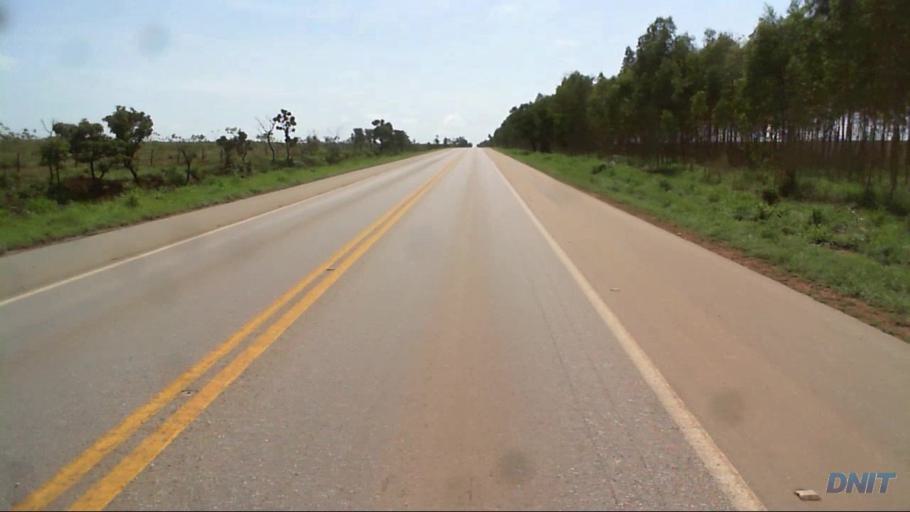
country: BR
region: Goias
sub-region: Barro Alto
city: Barro Alto
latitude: -15.2035
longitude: -48.7436
